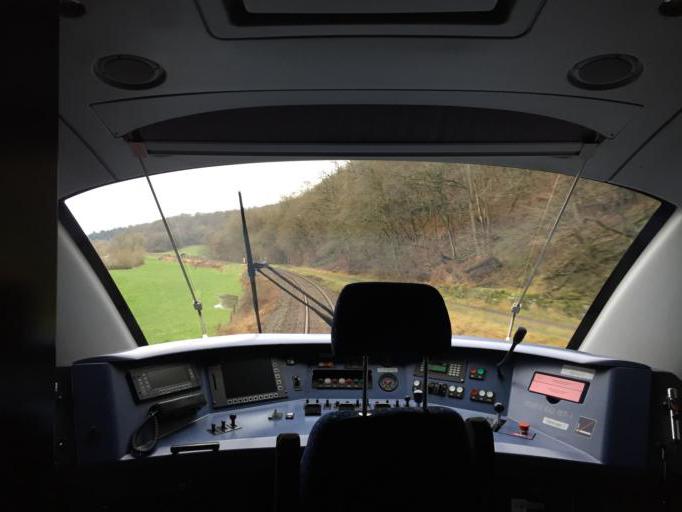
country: DE
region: Hesse
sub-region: Regierungsbezirk Kassel
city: Frankenau
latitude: 51.1156
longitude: 8.8605
